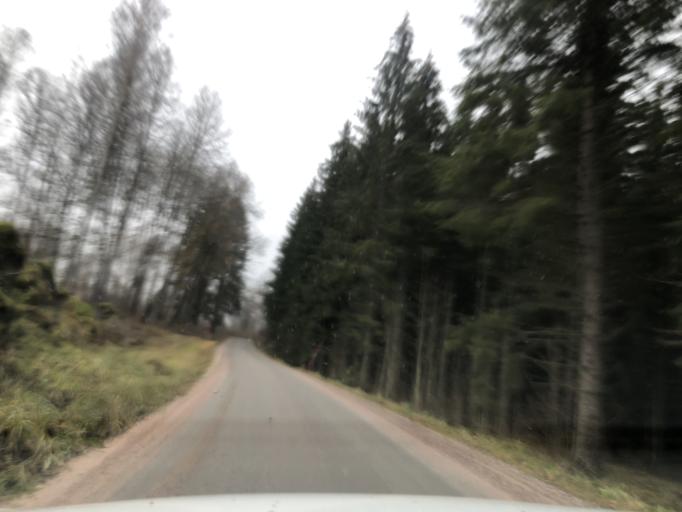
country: SE
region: Vaestra Goetaland
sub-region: Ulricehamns Kommun
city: Ulricehamn
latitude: 57.8469
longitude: 13.6363
